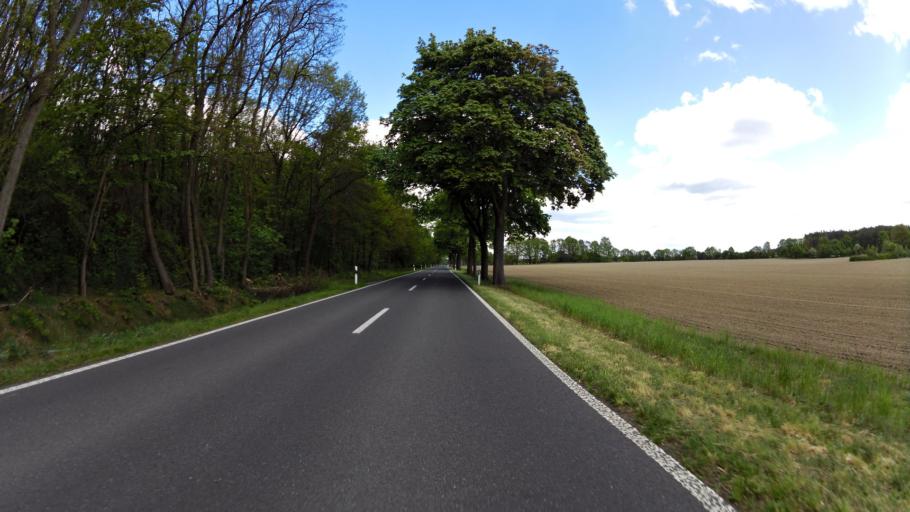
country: DE
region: Brandenburg
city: Rietz Neuendorf
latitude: 52.2494
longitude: 14.1238
